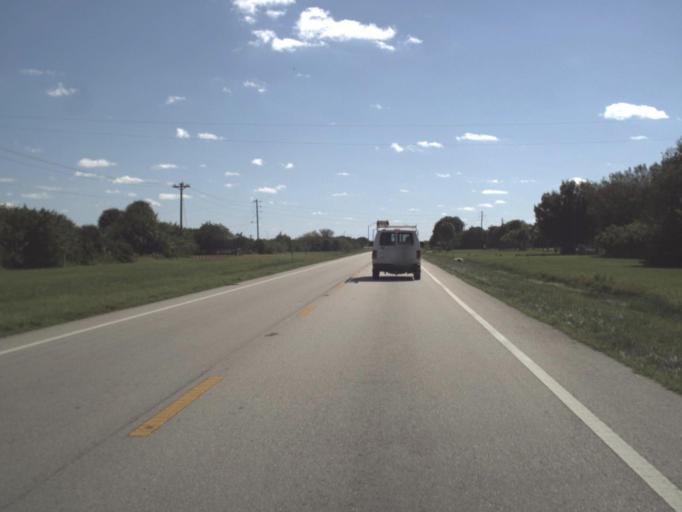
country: US
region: Florida
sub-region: Collier County
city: Immokalee
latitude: 26.4873
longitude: -81.4413
